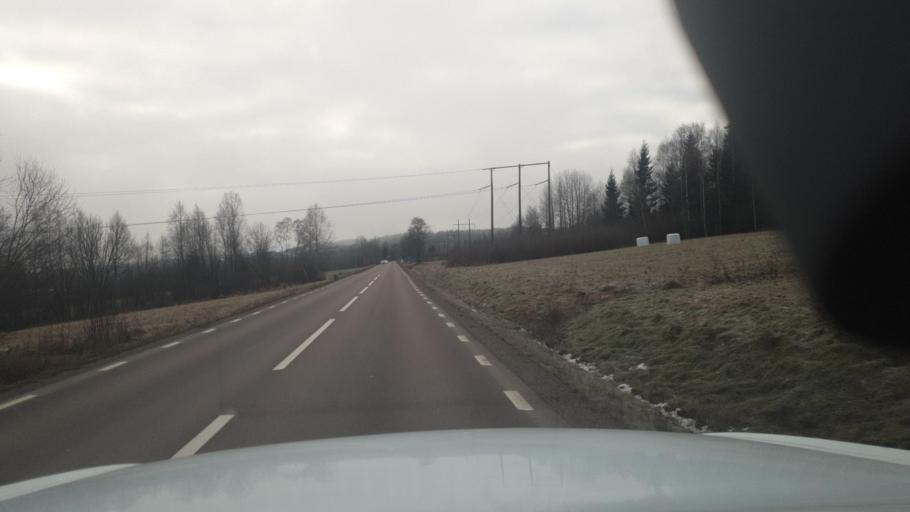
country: SE
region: Vaermland
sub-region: Torsby Kommun
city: Torsby
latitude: 59.9328
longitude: 12.8995
